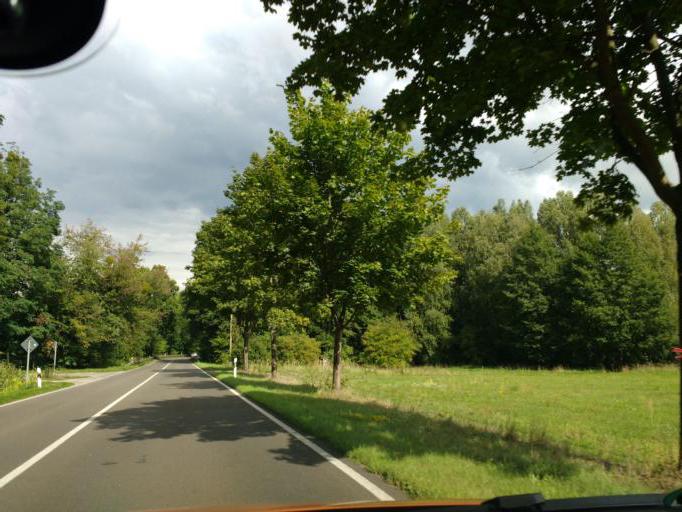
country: DE
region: Brandenburg
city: Marienwerder
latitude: 52.8555
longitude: 13.6150
